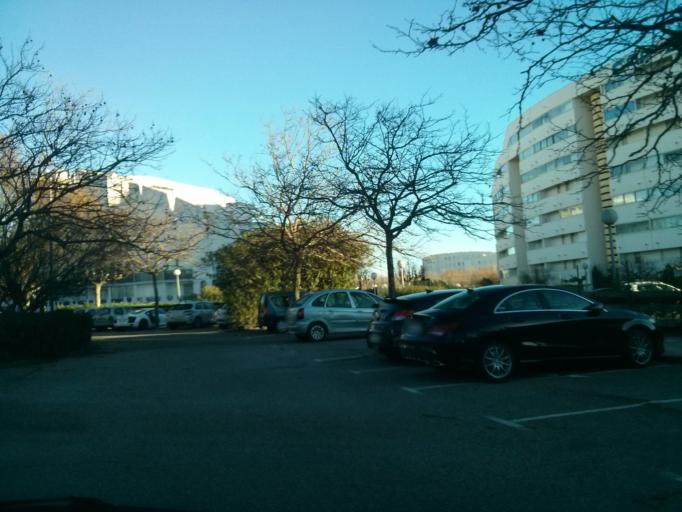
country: FR
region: Languedoc-Roussillon
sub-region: Departement de l'Herault
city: La Grande-Motte
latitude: 43.5602
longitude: 4.0685
